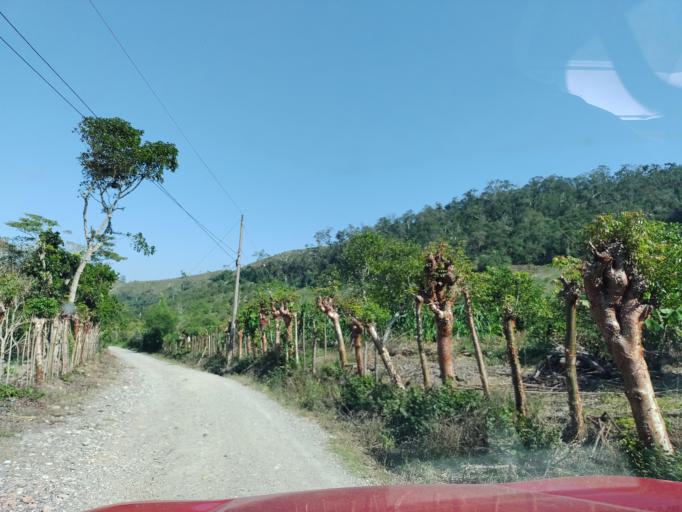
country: MX
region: Veracruz
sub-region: Papantla
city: Polutla
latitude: 20.4834
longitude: -97.1932
